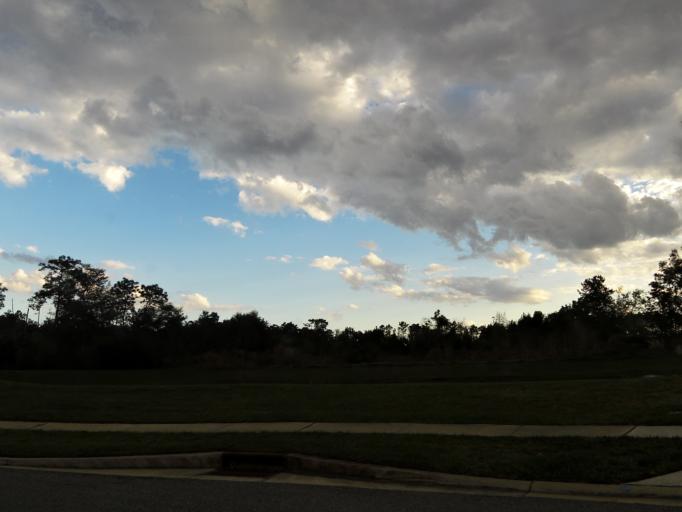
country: US
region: Florida
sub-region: Saint Johns County
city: Fruit Cove
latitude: 30.1714
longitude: -81.5660
